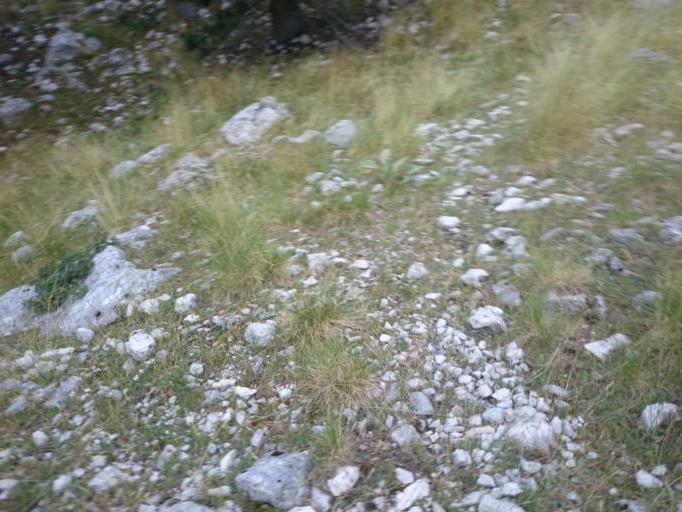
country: AL
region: Elbasan
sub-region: Rrethi i Gramshit
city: Kushove
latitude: 40.7241
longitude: 20.1427
